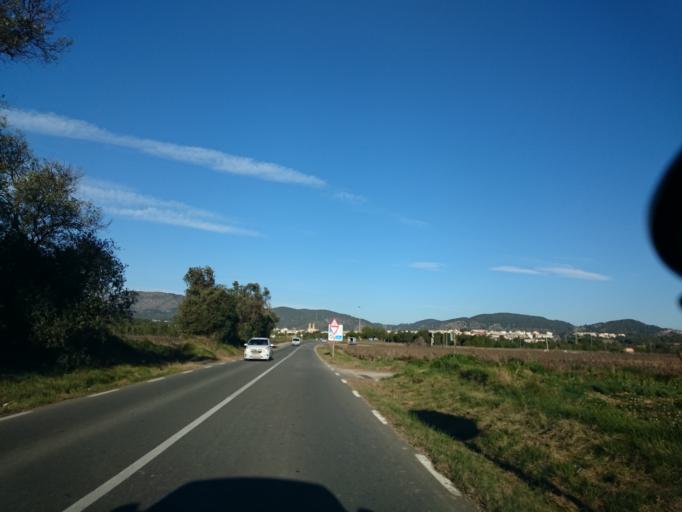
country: ES
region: Catalonia
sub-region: Provincia de Barcelona
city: Sant Pere de Ribes
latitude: 41.2482
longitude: 1.7874
